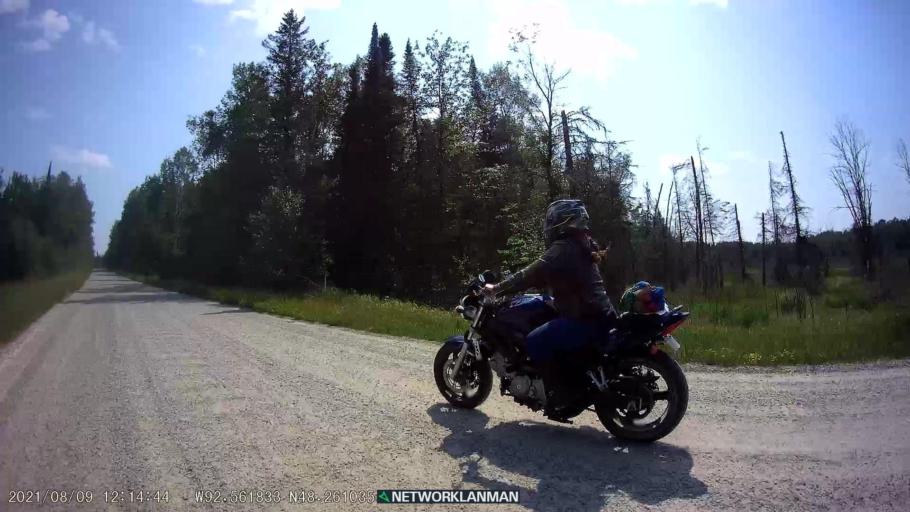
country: US
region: Minnesota
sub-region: Saint Louis County
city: Parkville
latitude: 48.2609
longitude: -92.5616
